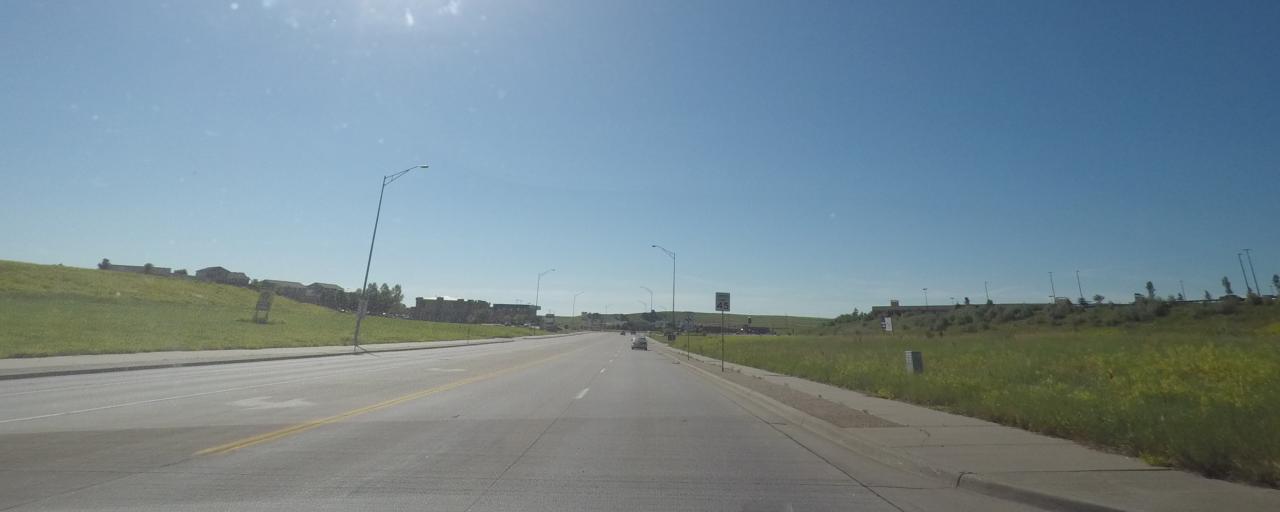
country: US
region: South Dakota
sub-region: Pennington County
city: Rapid City
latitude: 44.0360
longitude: -103.2173
